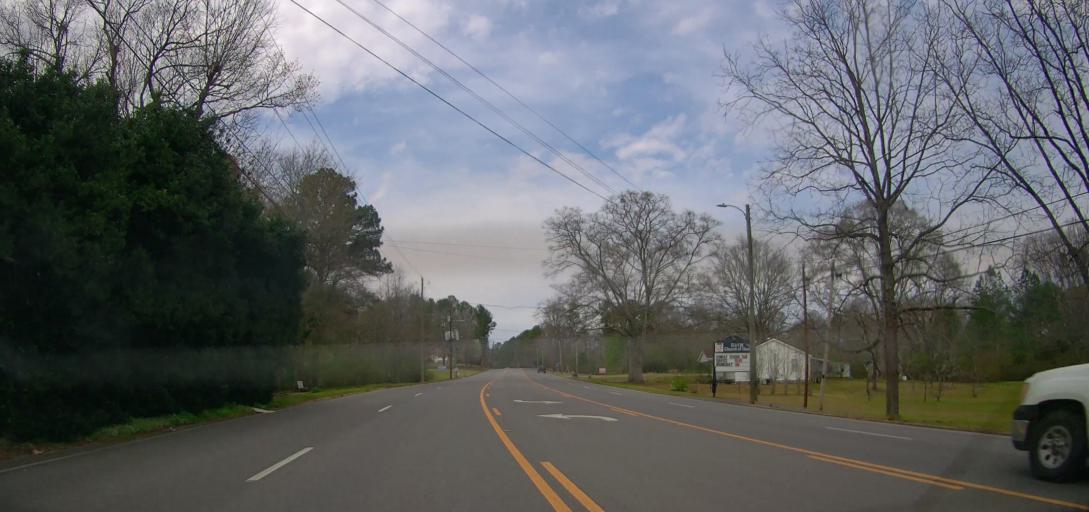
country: US
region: Alabama
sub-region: Marion County
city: Guin
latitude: 33.9787
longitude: -87.9175
